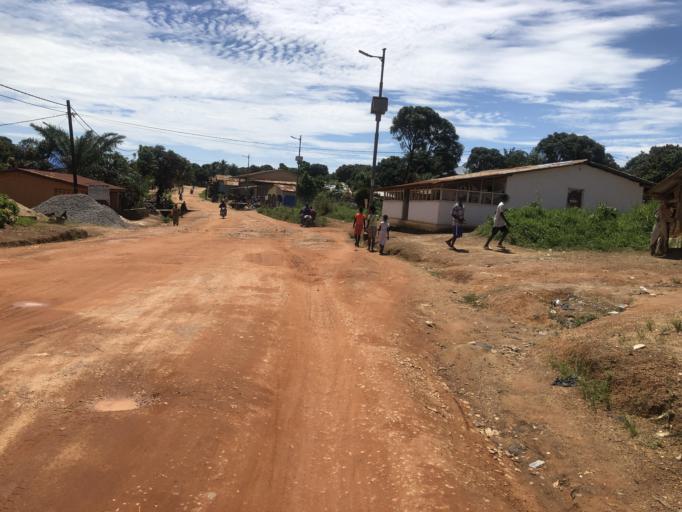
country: SL
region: Eastern Province
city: Koidu
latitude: 8.6400
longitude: -10.9595
